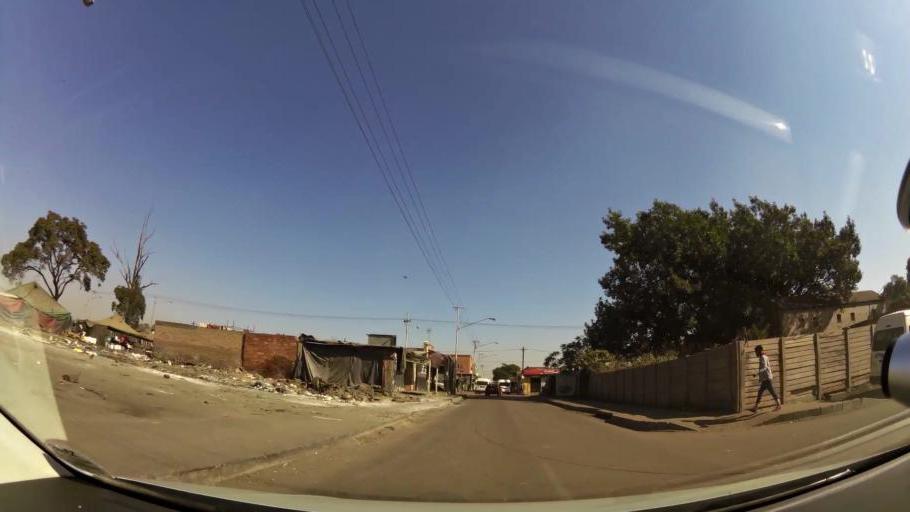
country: ZA
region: Gauteng
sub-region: City of Tshwane Metropolitan Municipality
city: Pretoria
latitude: -25.7407
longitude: 28.1759
